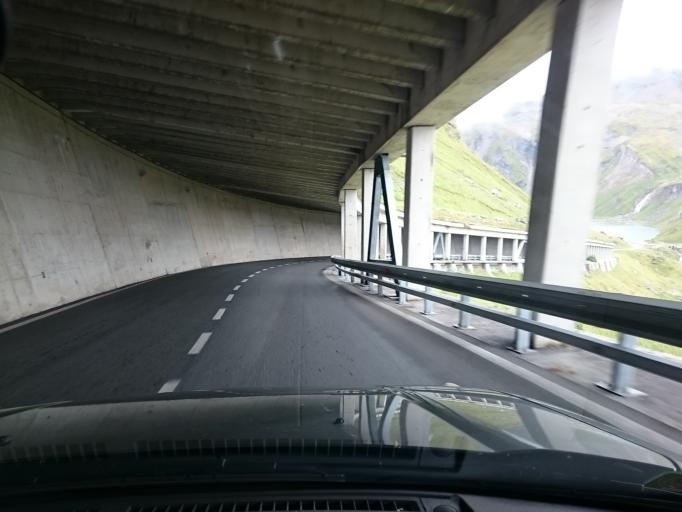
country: AT
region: Carinthia
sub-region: Politischer Bezirk Spittal an der Drau
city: Heiligenblut
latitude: 47.0747
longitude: 12.7604
